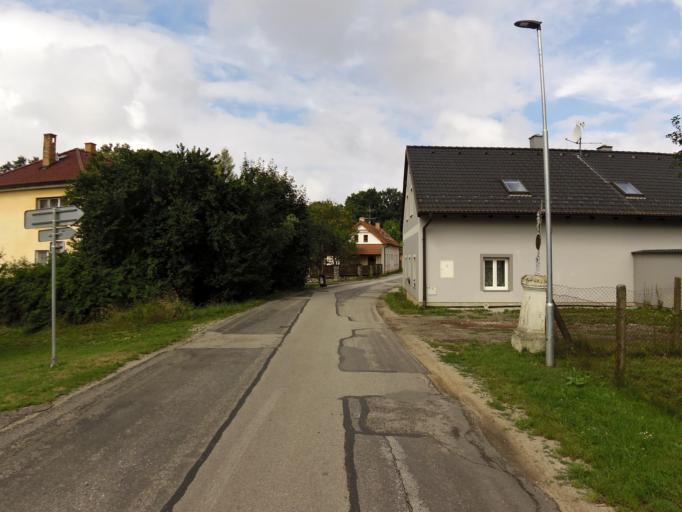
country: CZ
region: Jihocesky
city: Suchdol nad Luznici
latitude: 48.9054
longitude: 14.9118
